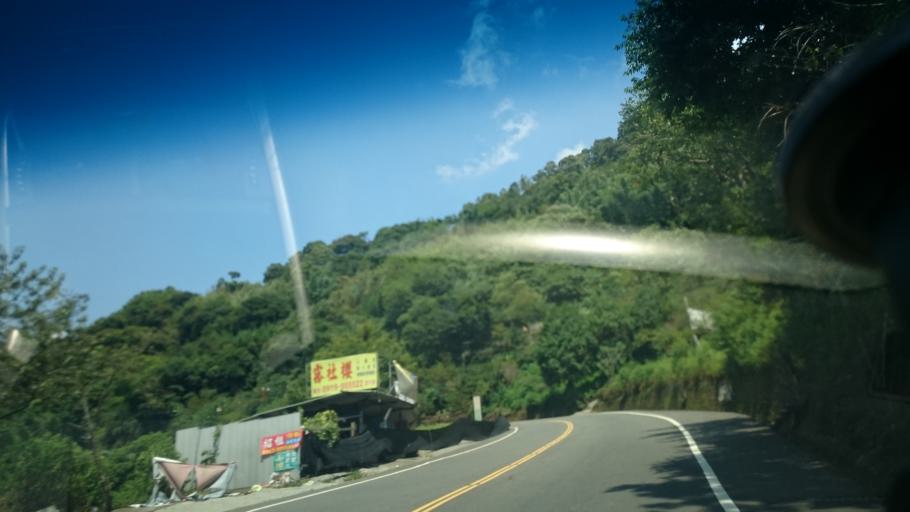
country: TW
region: Taiwan
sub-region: Nantou
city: Puli
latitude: 24.0166
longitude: 121.1269
